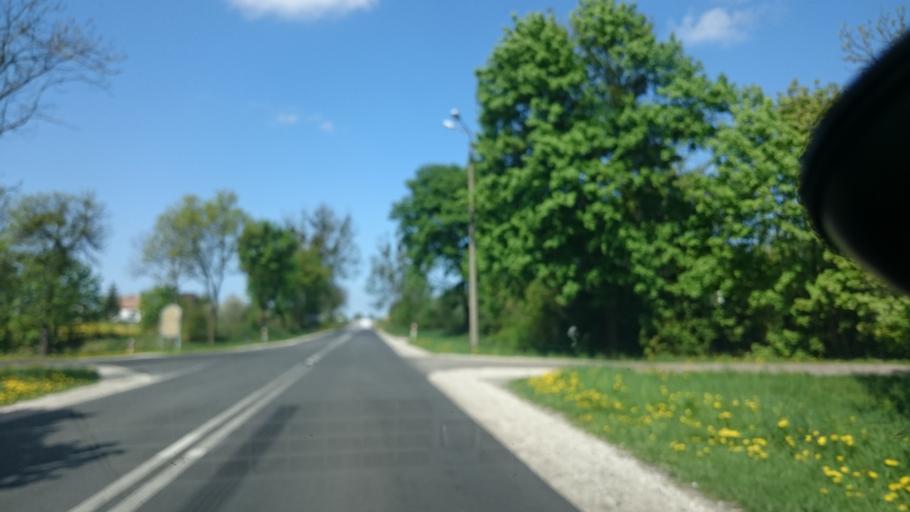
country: PL
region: Kujawsko-Pomorskie
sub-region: Powiat swiecki
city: Warlubie
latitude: 53.5968
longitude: 18.6242
